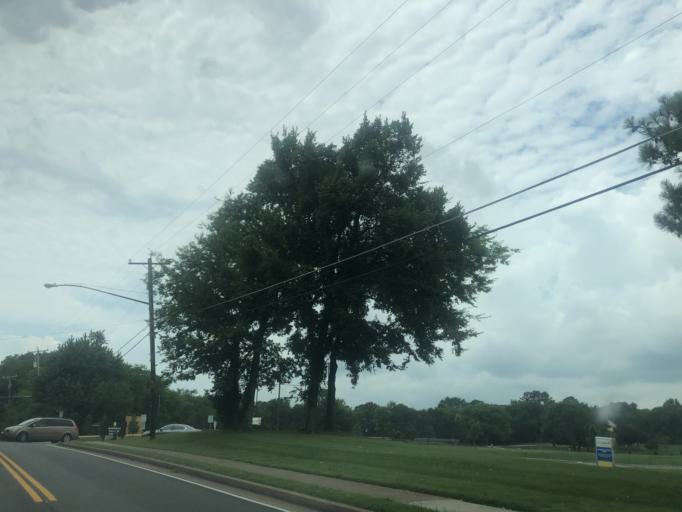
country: US
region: Tennessee
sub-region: Davidson County
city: Oak Hill
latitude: 36.0943
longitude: -86.8033
